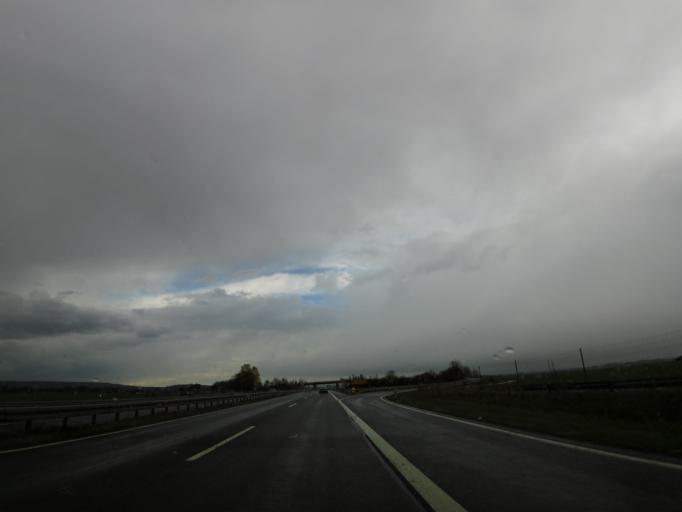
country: DE
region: Lower Saxony
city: Vienenburg
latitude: 51.9284
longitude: 10.5624
